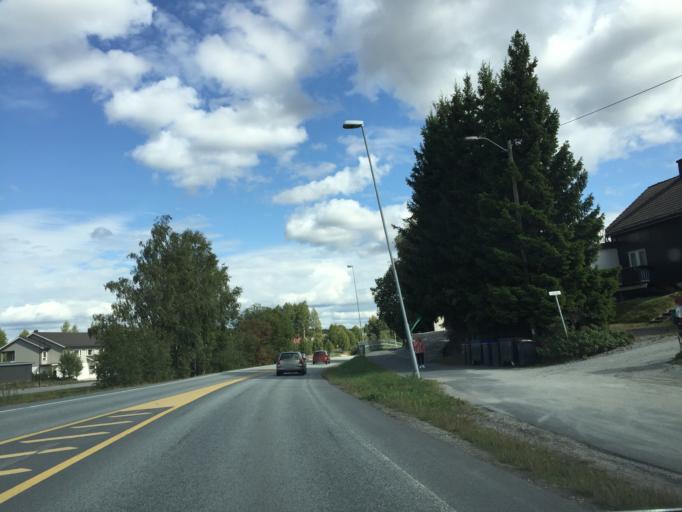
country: NO
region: Ostfold
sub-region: Spydeberg
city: Spydeberg
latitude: 59.6161
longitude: 11.0694
